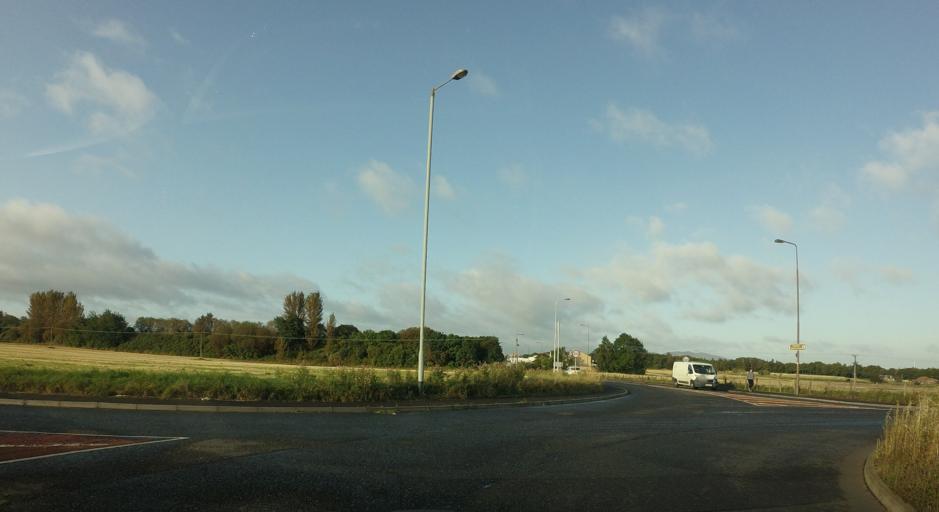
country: GB
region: Scotland
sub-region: East Lothian
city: Musselburgh
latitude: 55.9232
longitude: -3.0341
